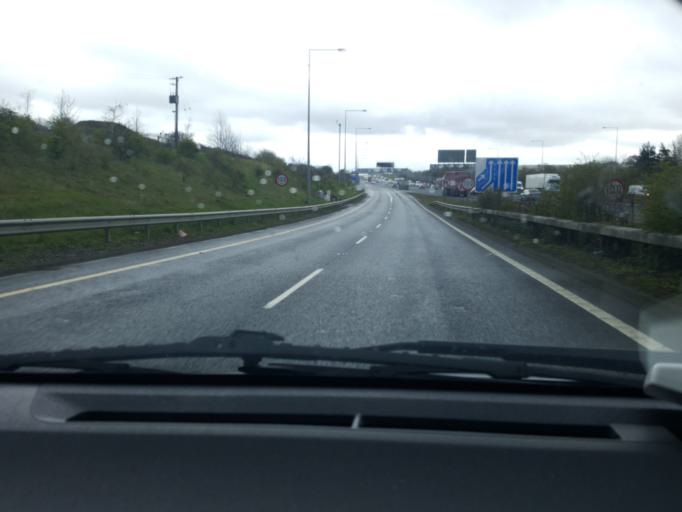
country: IE
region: Leinster
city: Ballymun
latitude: 53.4096
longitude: -6.2628
